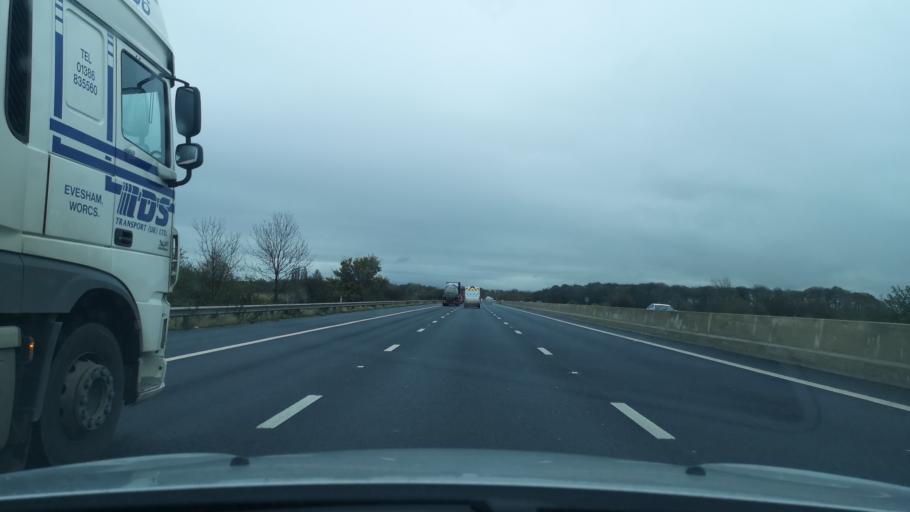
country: GB
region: England
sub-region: Doncaster
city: Norton
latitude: 53.6949
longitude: -1.1715
